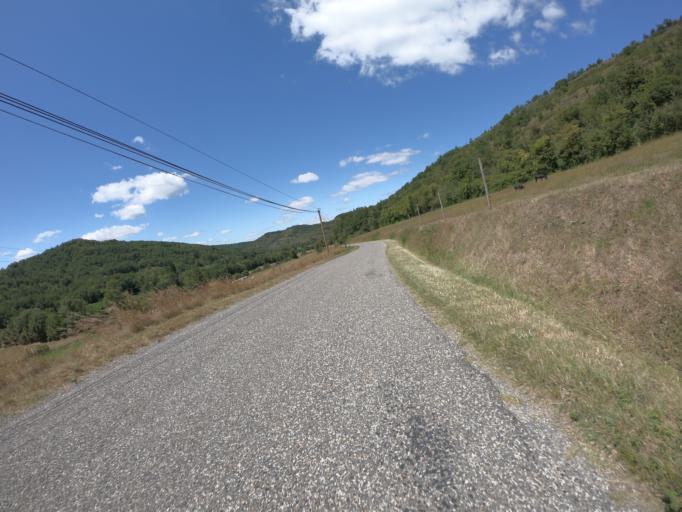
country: FR
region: Midi-Pyrenees
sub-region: Departement de l'Ariege
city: Mirepoix
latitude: 43.0484
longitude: 1.8216
